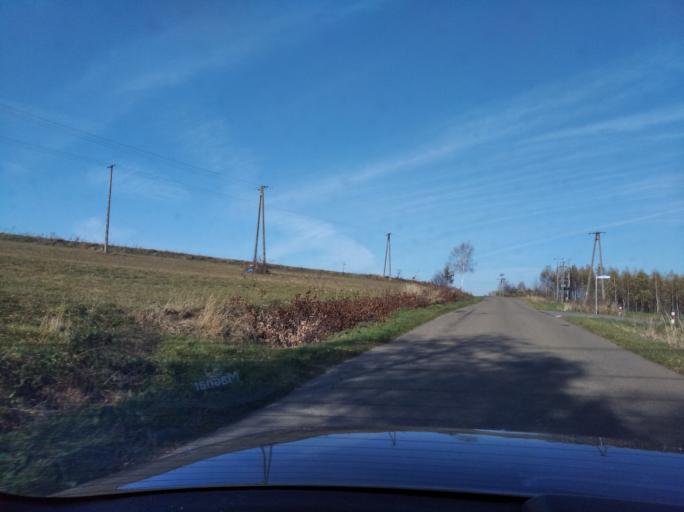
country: PL
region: Subcarpathian Voivodeship
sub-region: Powiat ropczycko-sedziszowski
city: Wielopole Skrzynskie
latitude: 49.9137
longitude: 21.5680
